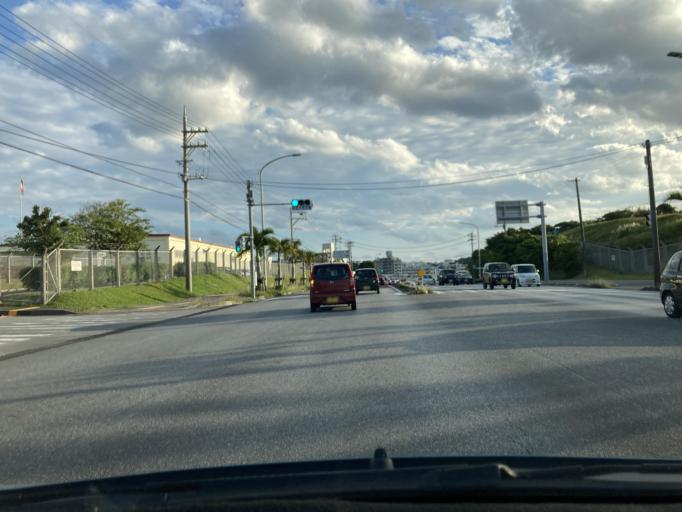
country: JP
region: Okinawa
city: Chatan
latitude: 26.2983
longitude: 127.7806
